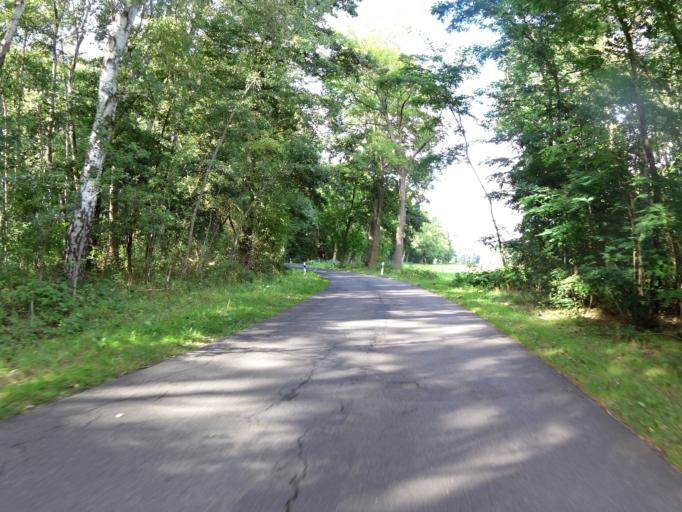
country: DE
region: Brandenburg
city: Storkow
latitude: 52.2321
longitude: 13.9330
